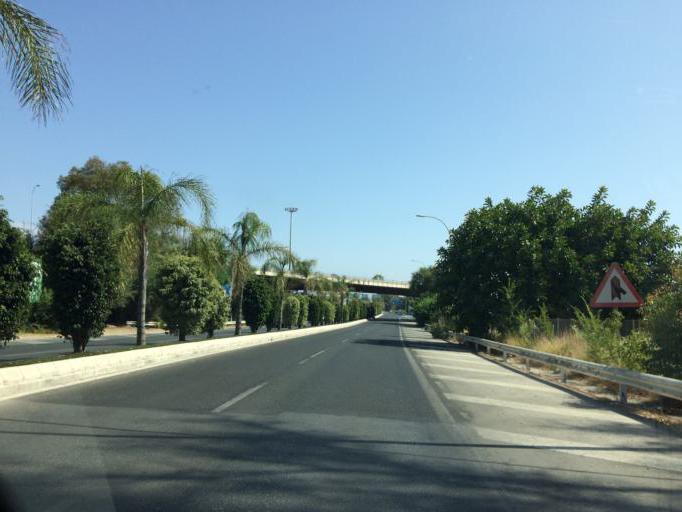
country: ES
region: Andalusia
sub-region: Provincia de Malaga
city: Torremolinos
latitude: 36.6471
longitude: -4.4893
